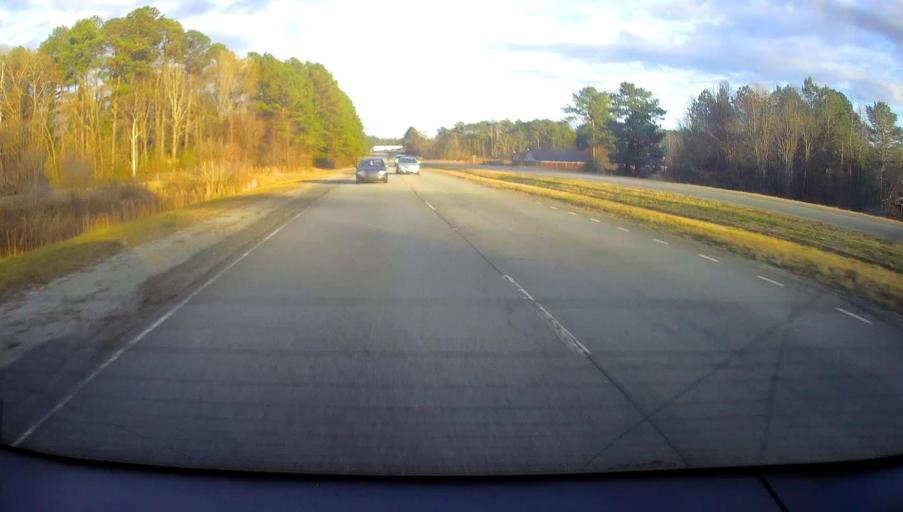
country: US
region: Alabama
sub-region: Etowah County
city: Glencoe
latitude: 33.9727
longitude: -85.9594
